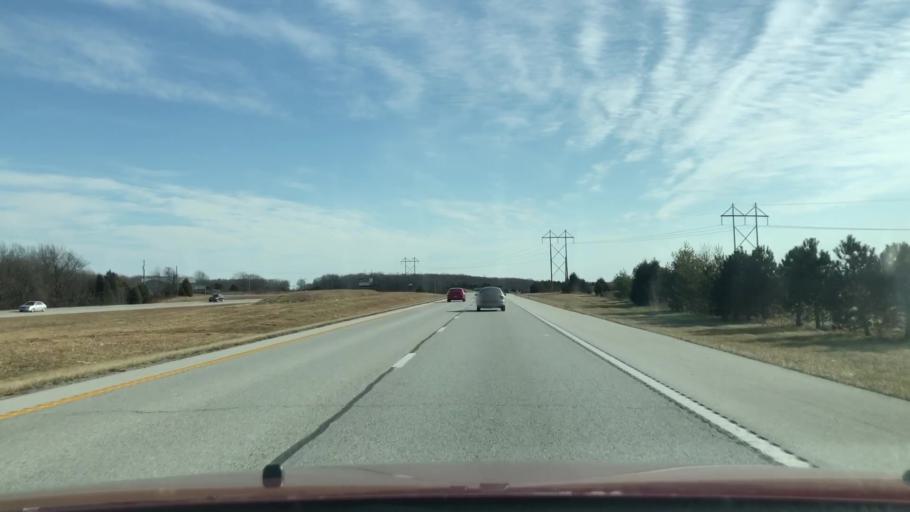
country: US
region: Missouri
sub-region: Webster County
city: Seymour
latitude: 37.1178
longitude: -92.6831
